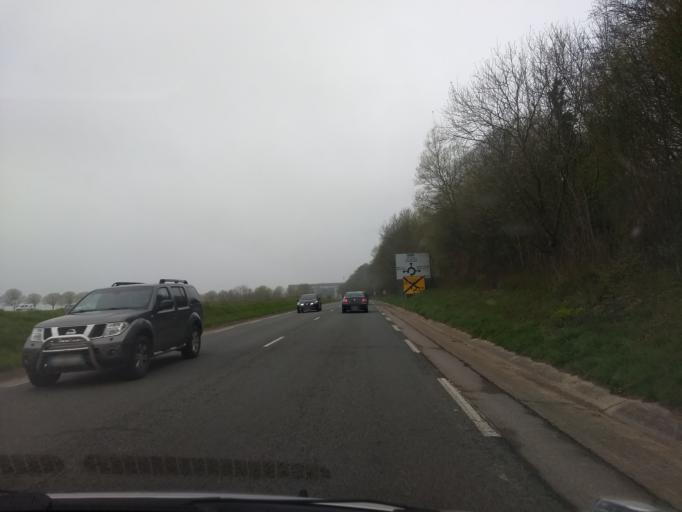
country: FR
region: Nord-Pas-de-Calais
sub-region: Departement du Pas-de-Calais
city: Verton
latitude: 50.4140
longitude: 1.6712
